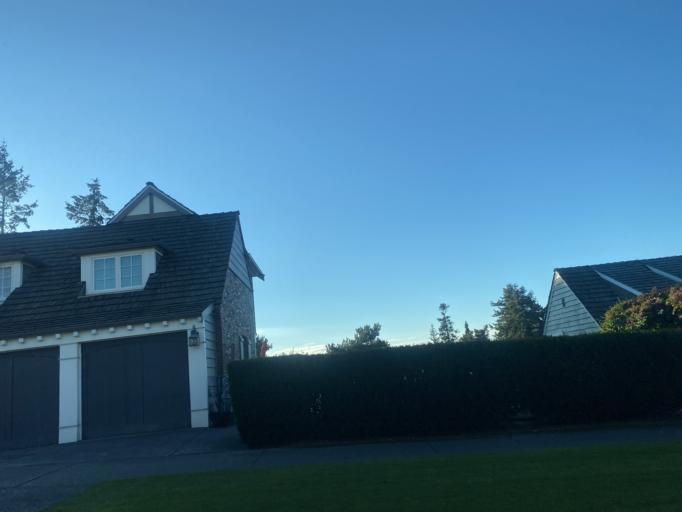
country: US
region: Washington
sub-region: King County
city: Seattle
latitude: 47.6470
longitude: -122.4120
